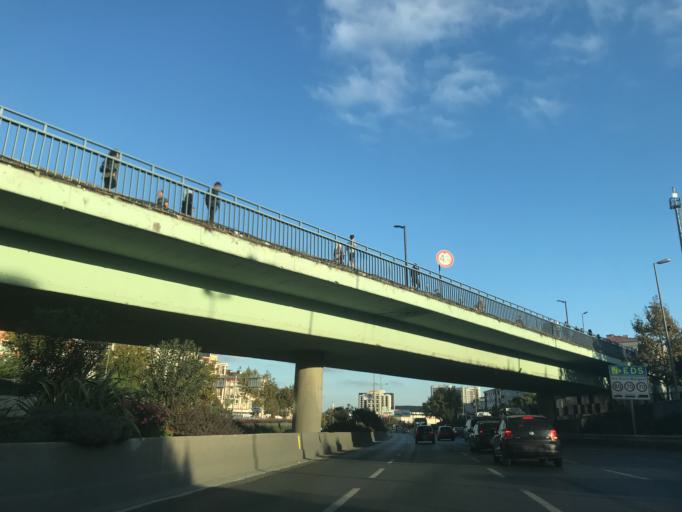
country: TR
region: Istanbul
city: Esenler
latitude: 41.0479
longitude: 28.8768
